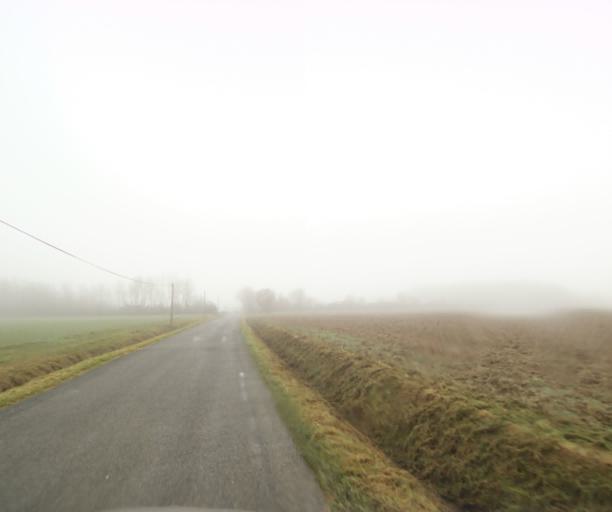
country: FR
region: Midi-Pyrenees
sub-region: Departement du Tarn-et-Garonne
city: Nohic
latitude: 43.8634
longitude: 1.4401
